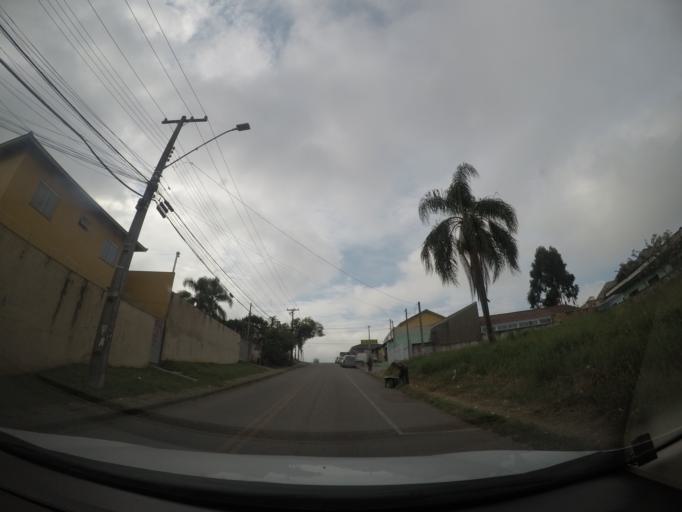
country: BR
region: Parana
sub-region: Colombo
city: Colombo
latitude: -25.3539
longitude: -49.2083
